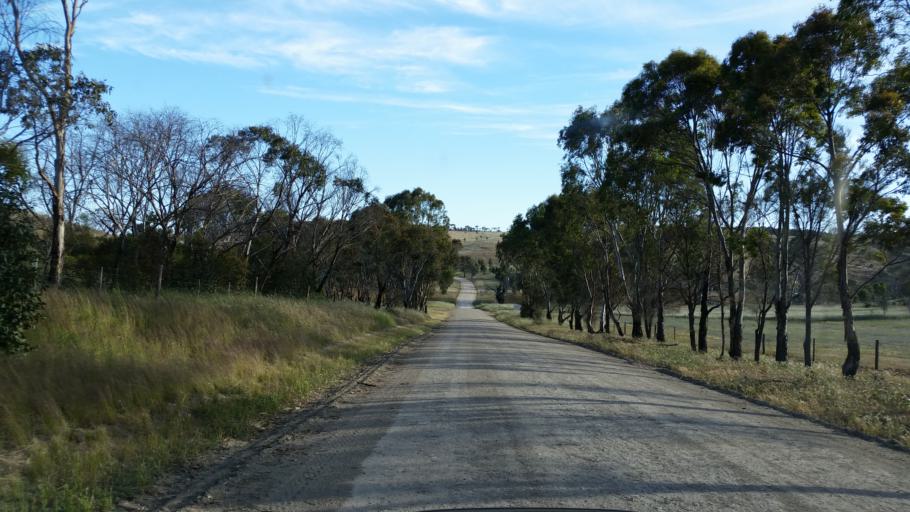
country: AU
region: South Australia
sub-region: Barossa
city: Angaston
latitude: -34.7003
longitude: 139.1688
